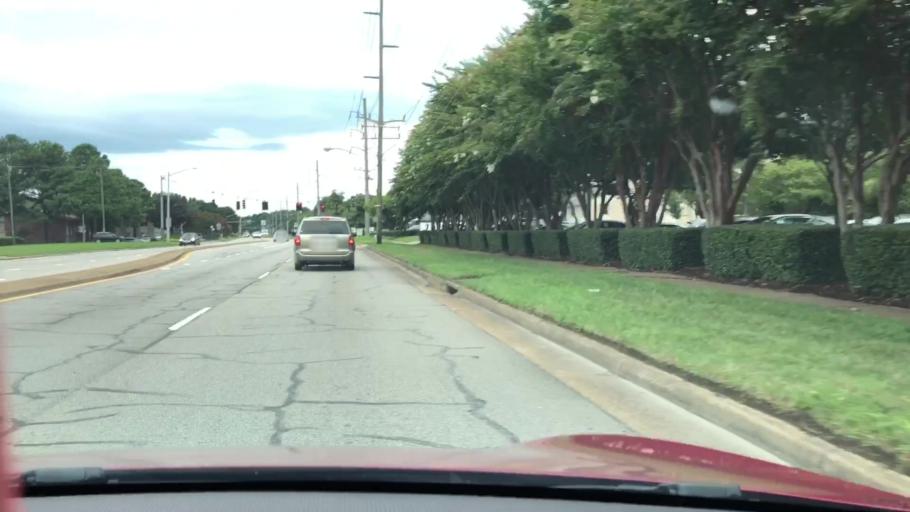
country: US
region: Virginia
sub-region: City of Virginia Beach
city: Virginia Beach
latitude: 36.8602
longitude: -76.0266
